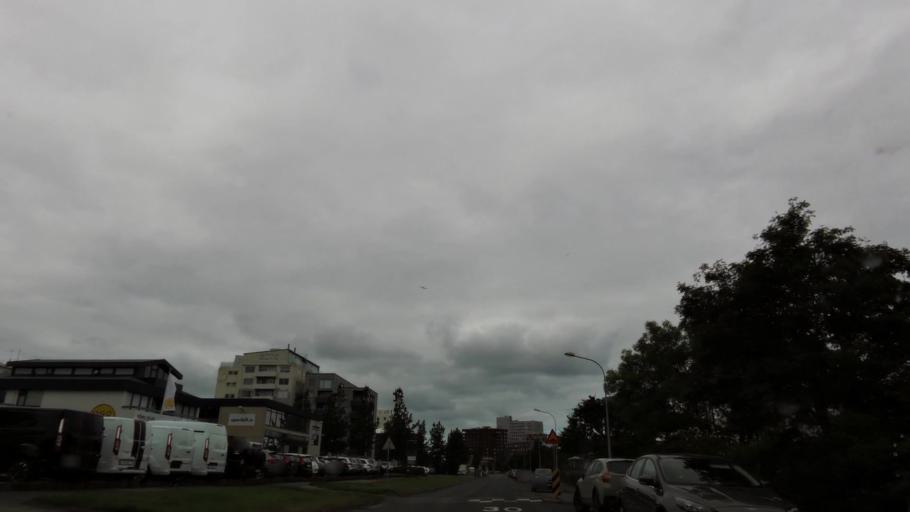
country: IS
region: Capital Region
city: Reykjavik
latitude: 64.1424
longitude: -21.8988
